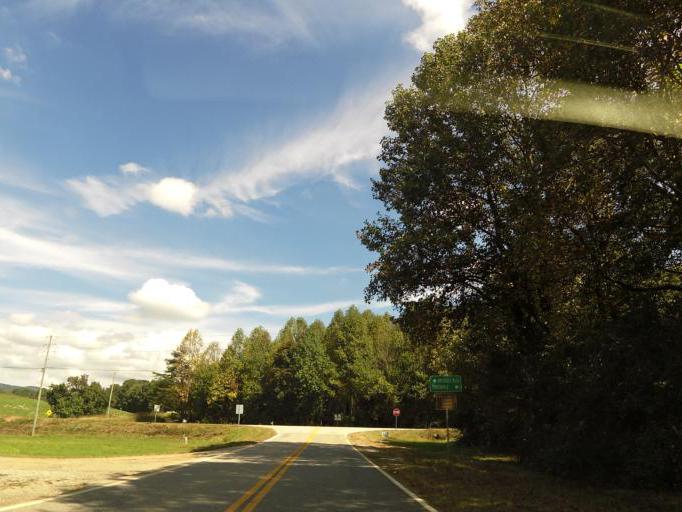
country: US
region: Georgia
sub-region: Dawson County
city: Dawsonville
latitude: 34.5254
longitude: -84.2528
